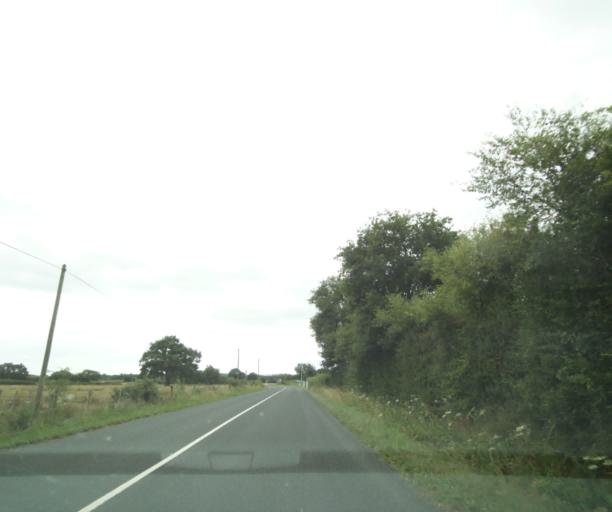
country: FR
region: Pays de la Loire
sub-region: Departement de la Sarthe
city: Precigne
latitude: 47.7538
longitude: -0.3051
